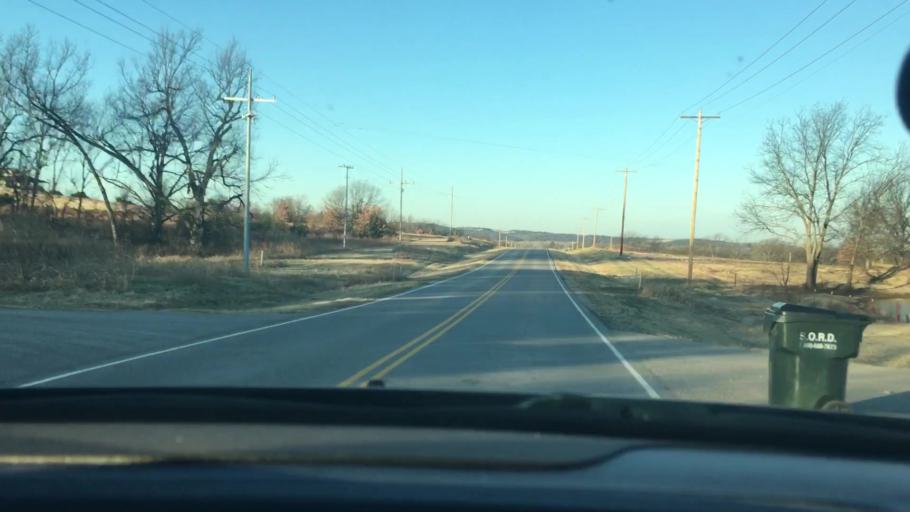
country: US
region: Oklahoma
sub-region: Murray County
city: Davis
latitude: 34.4774
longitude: -97.1174
